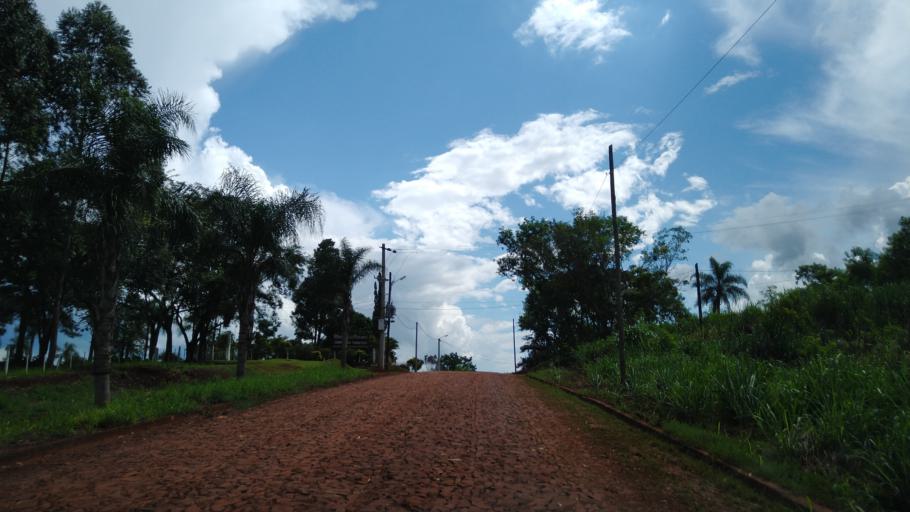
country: AR
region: Misiones
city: Puerto Libertad
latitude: -25.9657
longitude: -54.6023
